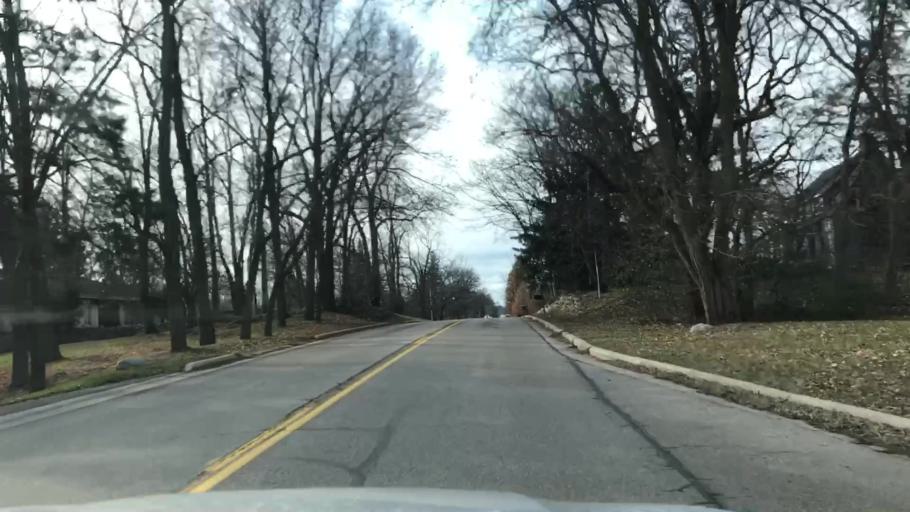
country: US
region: Michigan
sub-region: Wayne County
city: Northville
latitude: 42.4517
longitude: -83.4900
